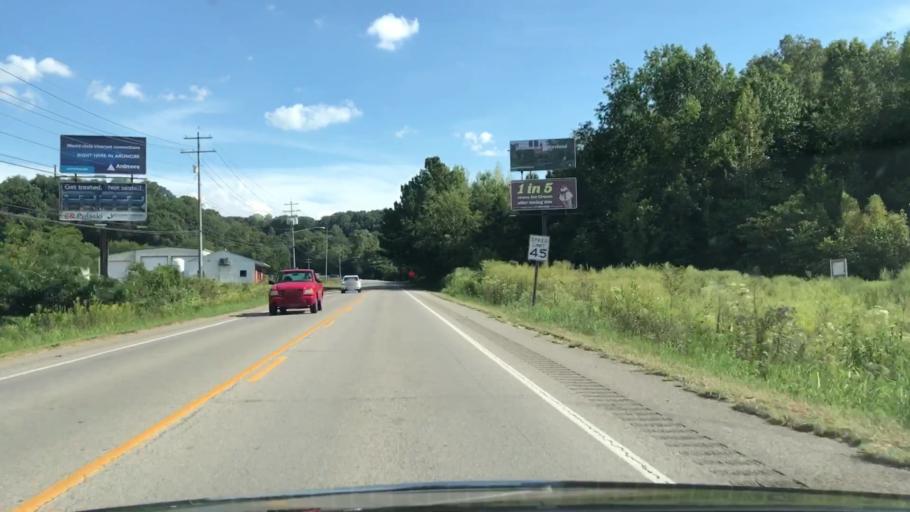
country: US
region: Alabama
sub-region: Limestone County
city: Ardmore
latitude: 35.0095
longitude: -86.8763
